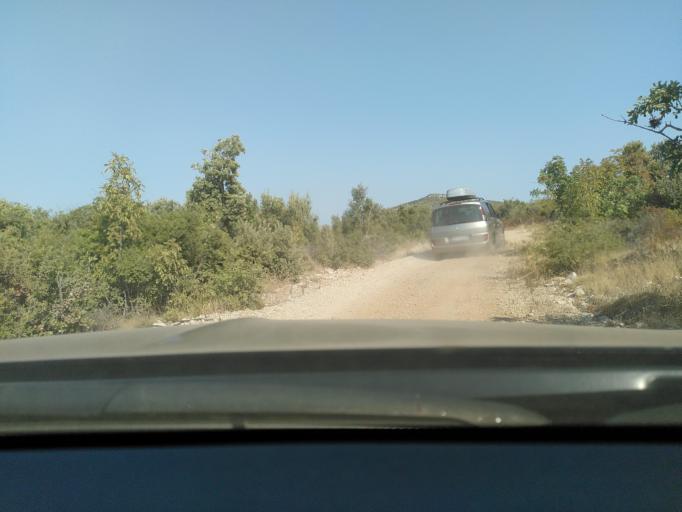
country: HR
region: Splitsko-Dalmatinska
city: Stari Grad
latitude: 43.1602
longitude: 16.5588
